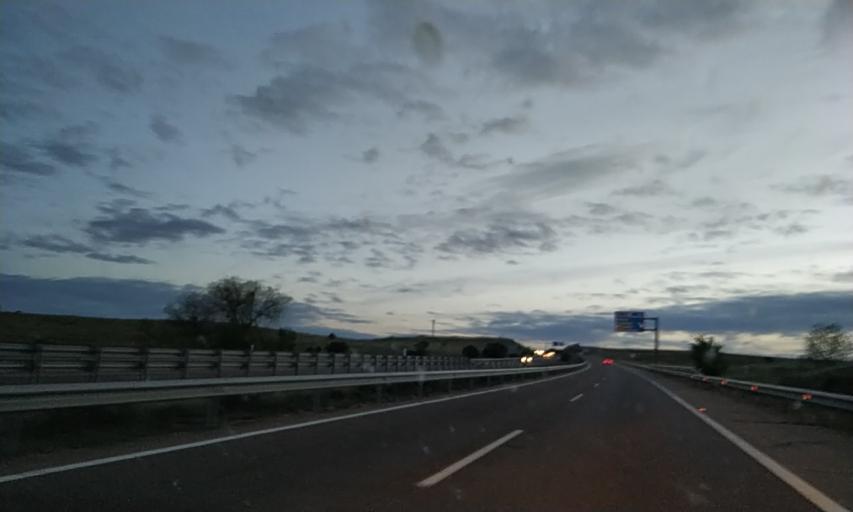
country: ES
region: Extremadura
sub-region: Provincia de Badajoz
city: Badajoz
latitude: 38.9145
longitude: -6.9869
